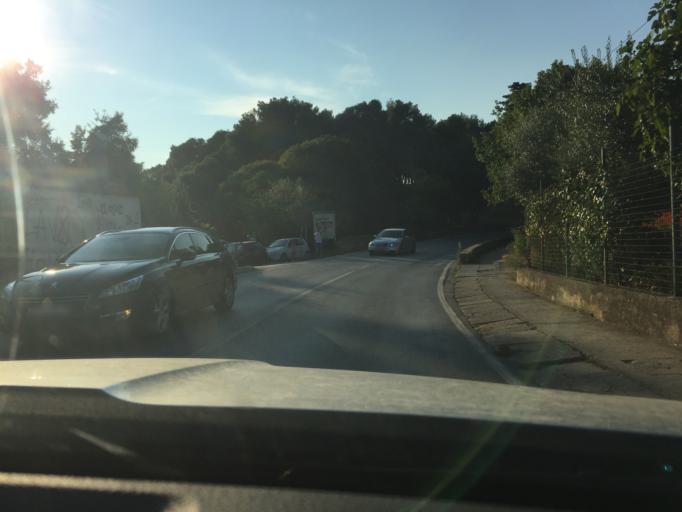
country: HR
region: Zadarska
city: Zadar
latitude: 44.1209
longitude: 15.2337
